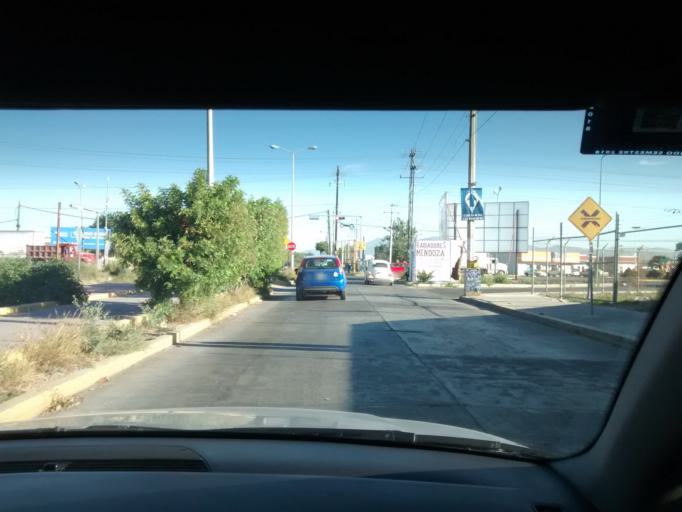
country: MX
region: Puebla
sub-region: Santiago Miahuatlan
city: San Isidro Vista Hermosa
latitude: 18.4834
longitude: -97.4136
